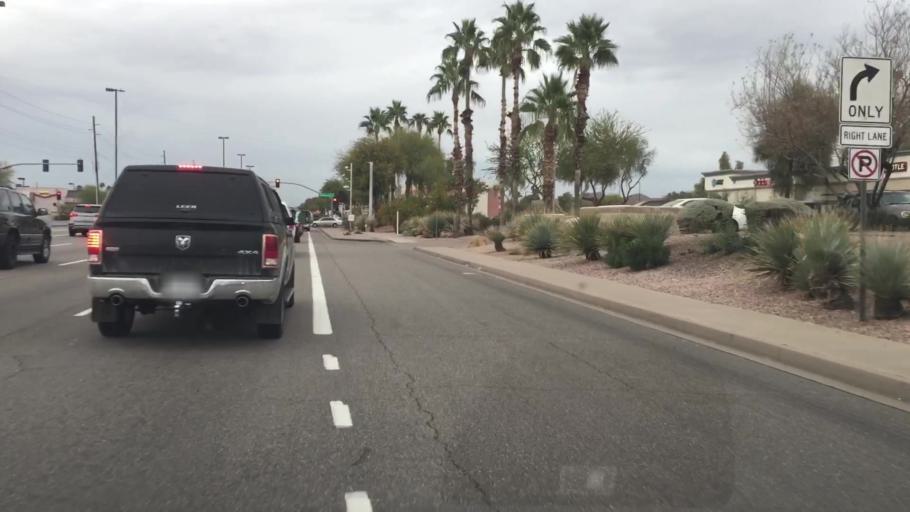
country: US
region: Arizona
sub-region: Maricopa County
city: Gilbert
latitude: 33.3893
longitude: -111.6846
